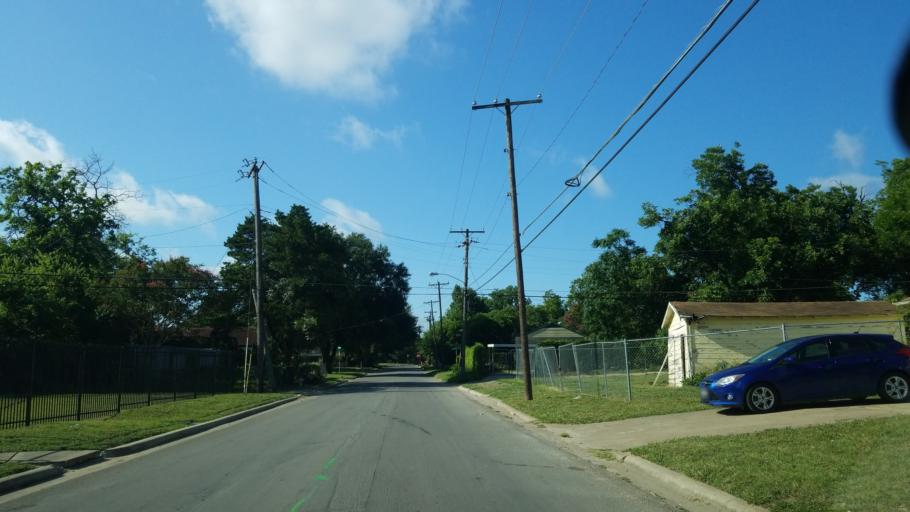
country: US
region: Texas
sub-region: Dallas County
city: Dallas
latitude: 32.7189
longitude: -96.8002
